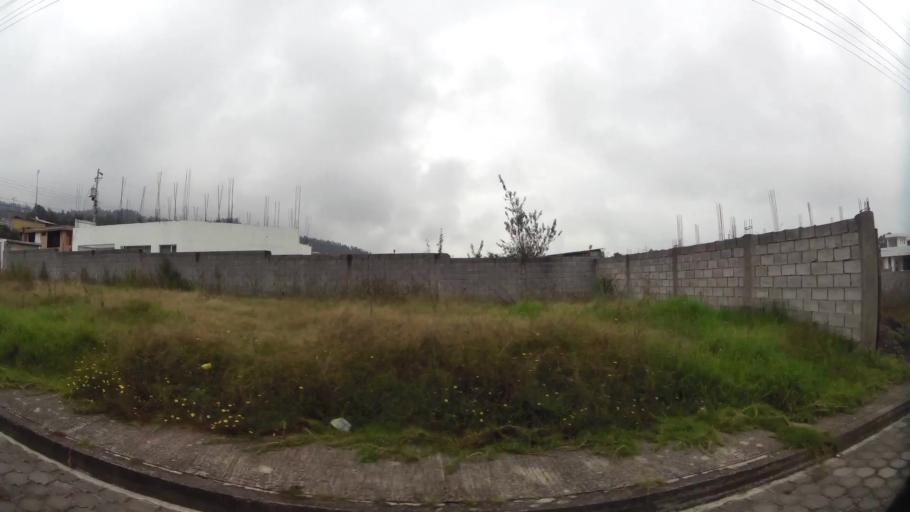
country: EC
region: Pichincha
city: Quito
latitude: -0.2683
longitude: -78.4764
